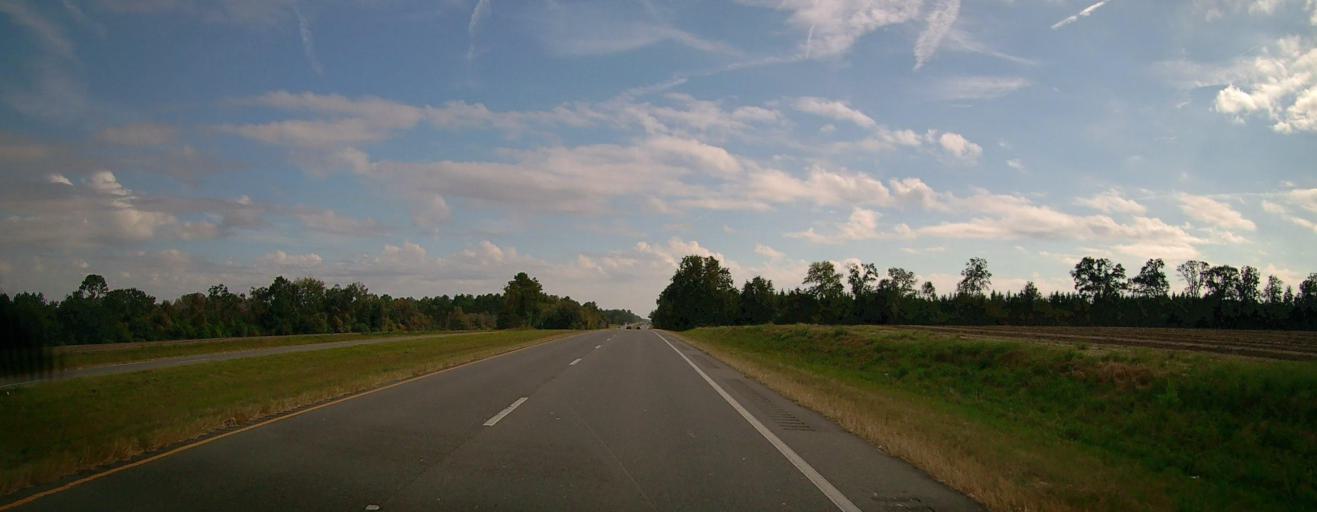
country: US
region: Georgia
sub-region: Thomas County
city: Meigs
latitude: 31.0248
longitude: -84.0597
